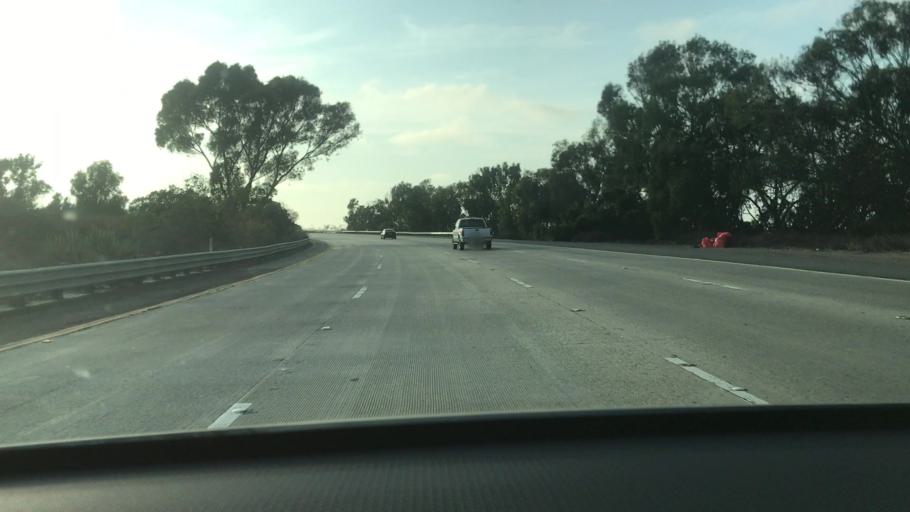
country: US
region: California
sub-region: San Diego County
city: Camp Pendleton South
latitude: 33.2370
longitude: -117.4064
